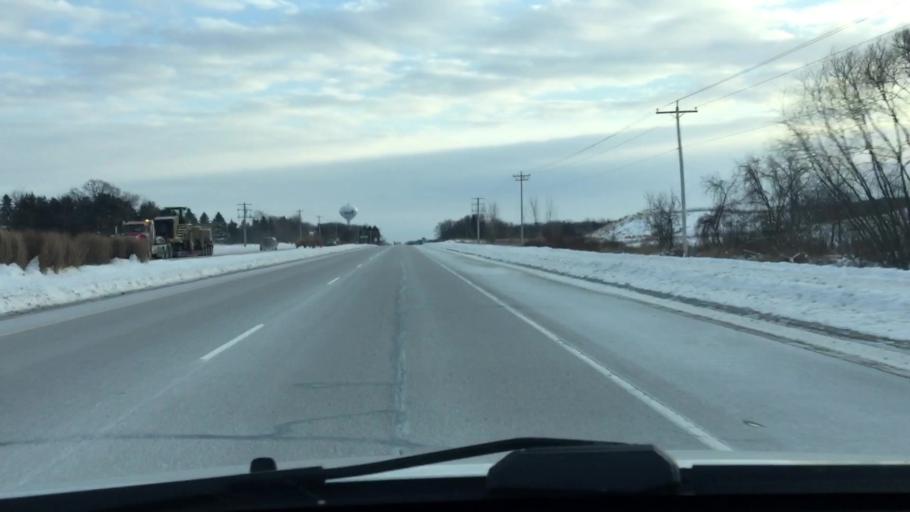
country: US
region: Wisconsin
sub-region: Waukesha County
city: Sussex
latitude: 43.1270
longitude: -88.2443
